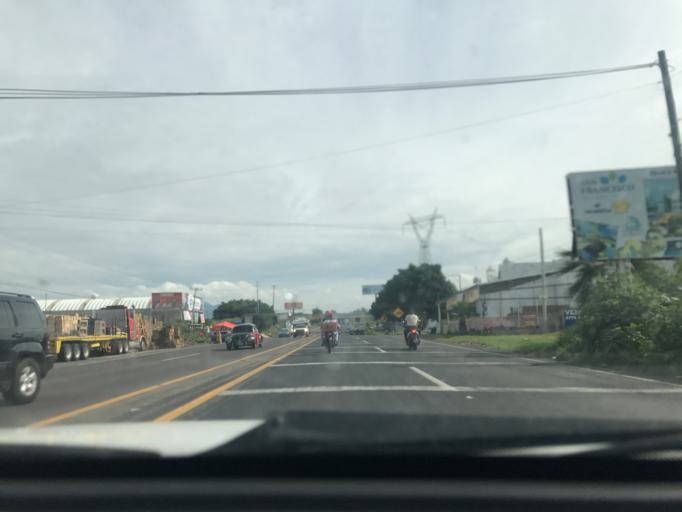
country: MX
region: Morelos
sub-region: Atlatlahucan
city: Colonia San Francisco
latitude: 18.8914
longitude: -98.9127
